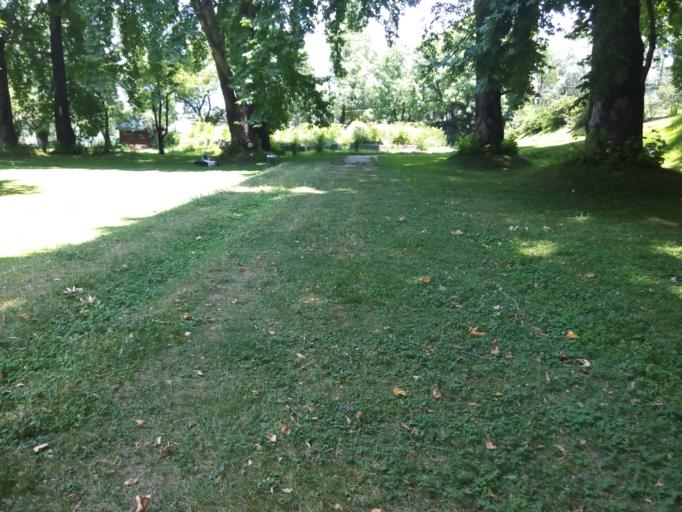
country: IN
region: Kashmir
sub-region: Srinagar
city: Srinagar
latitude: 34.1262
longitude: 74.8828
